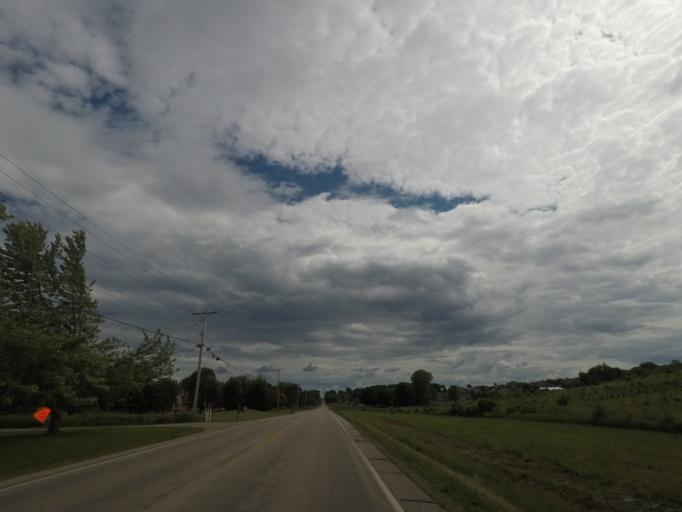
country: US
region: Wisconsin
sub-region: Dane County
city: Belleville
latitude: 42.8435
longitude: -89.5254
